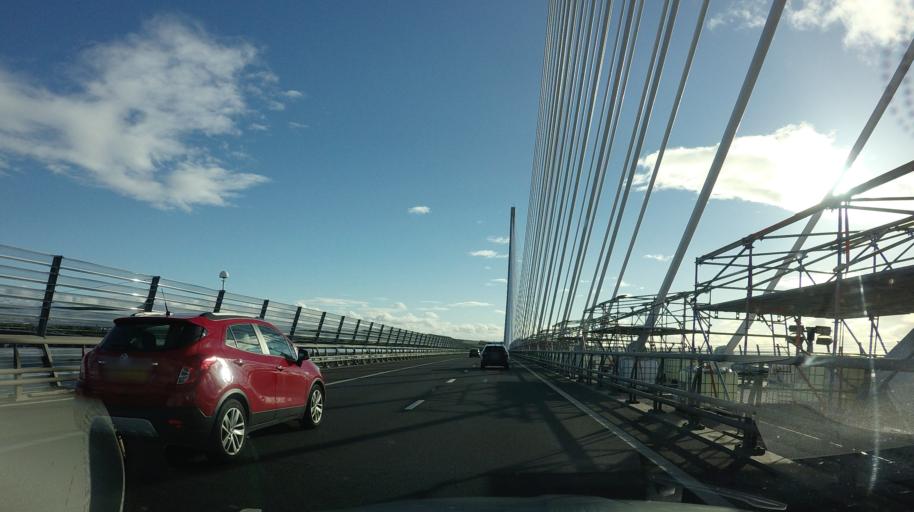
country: GB
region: Scotland
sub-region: Edinburgh
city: Queensferry
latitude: 56.0034
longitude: -3.4132
